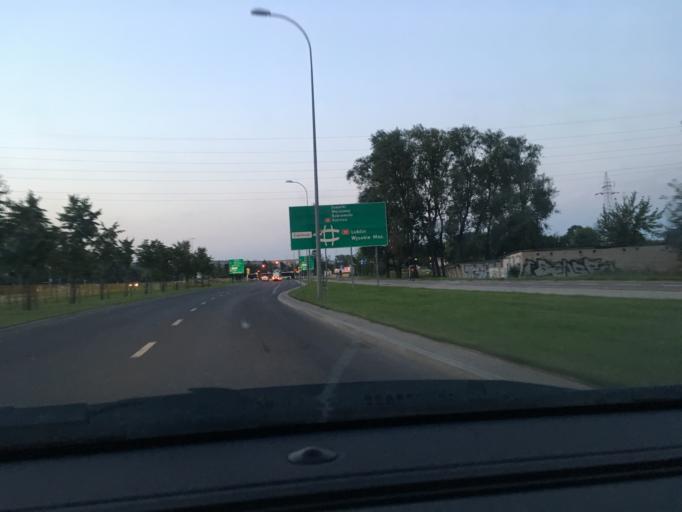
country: PL
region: Podlasie
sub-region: Bialystok
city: Bialystok
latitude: 53.1230
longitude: 23.1806
